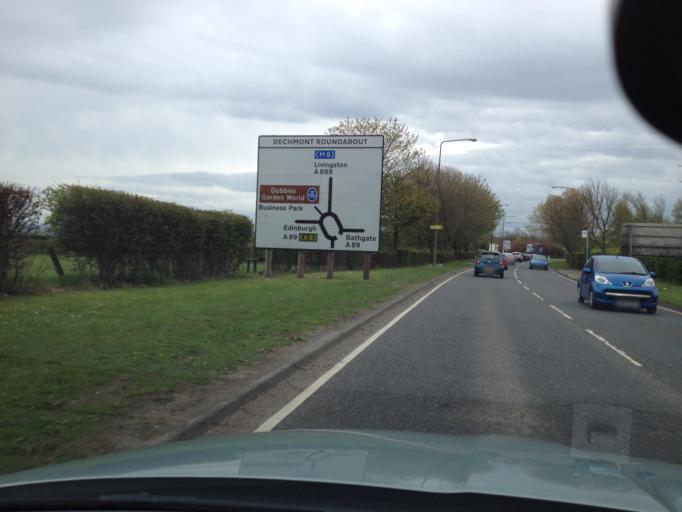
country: GB
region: Scotland
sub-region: West Lothian
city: Livingston
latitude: 55.9225
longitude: -3.5279
